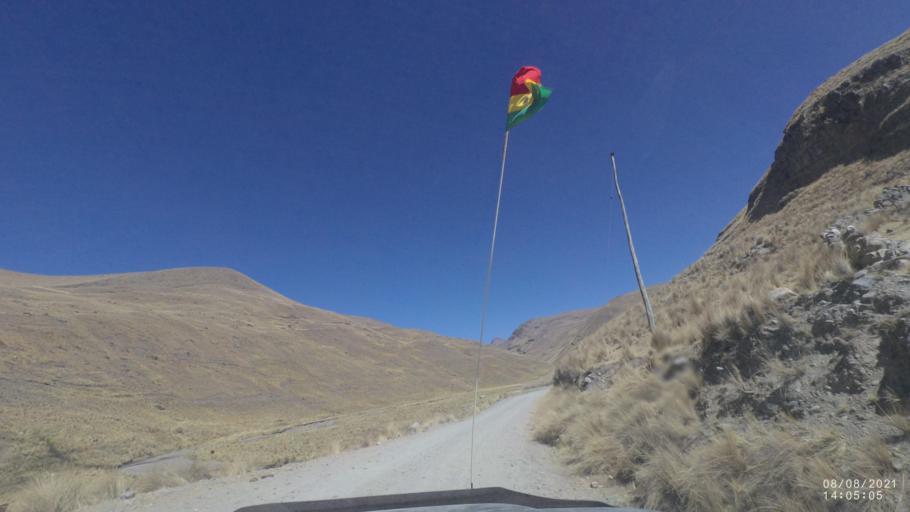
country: BO
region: Cochabamba
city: Sipe Sipe
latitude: -17.1149
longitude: -66.4390
